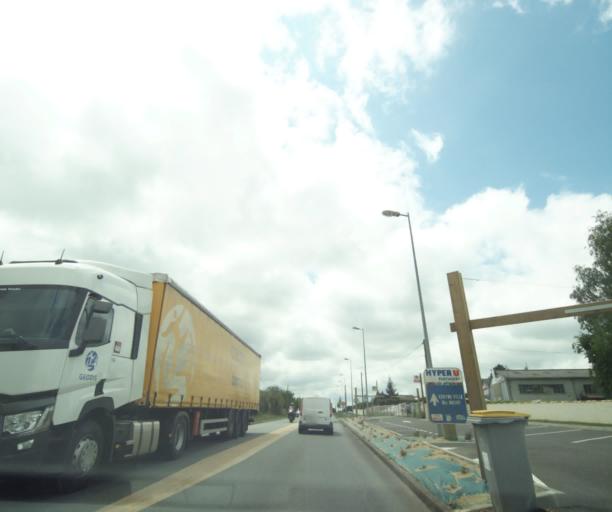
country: FR
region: Poitou-Charentes
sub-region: Departement des Deux-Sevres
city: Viennay
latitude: 46.6939
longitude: -0.2429
